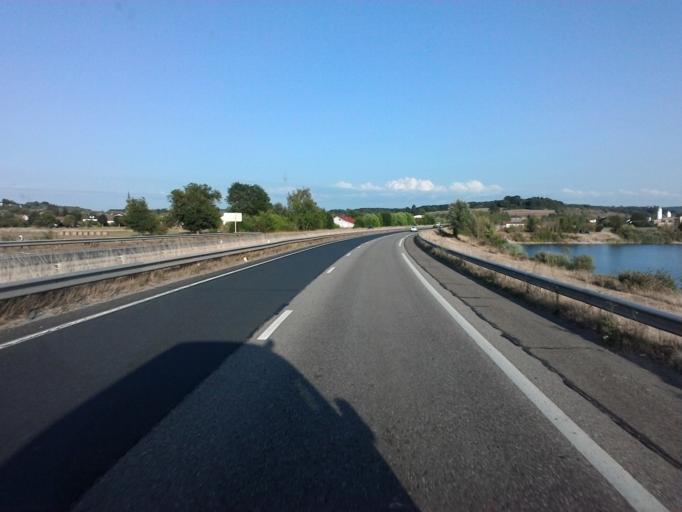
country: FR
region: Lorraine
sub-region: Departement des Vosges
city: Chavelot
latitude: 48.2241
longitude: 6.4457
